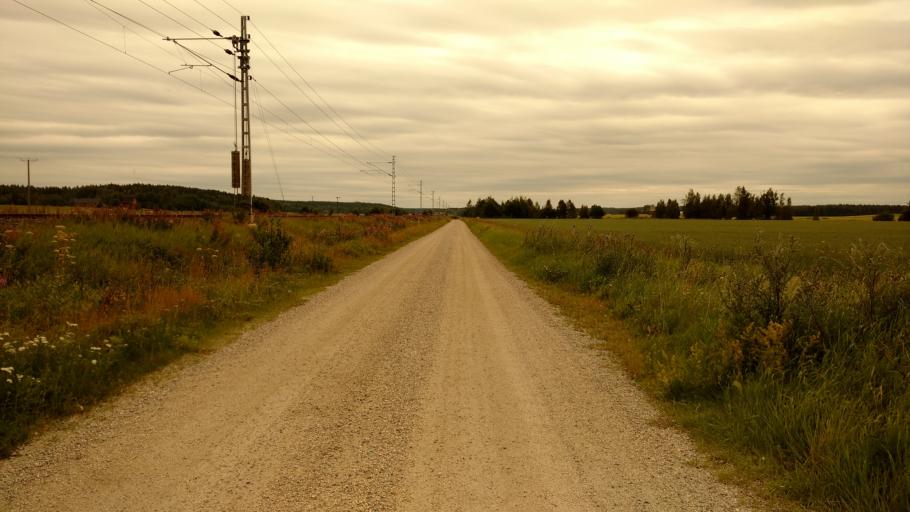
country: FI
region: Varsinais-Suomi
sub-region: Turku
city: Paimio
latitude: 60.4208
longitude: 22.8290
